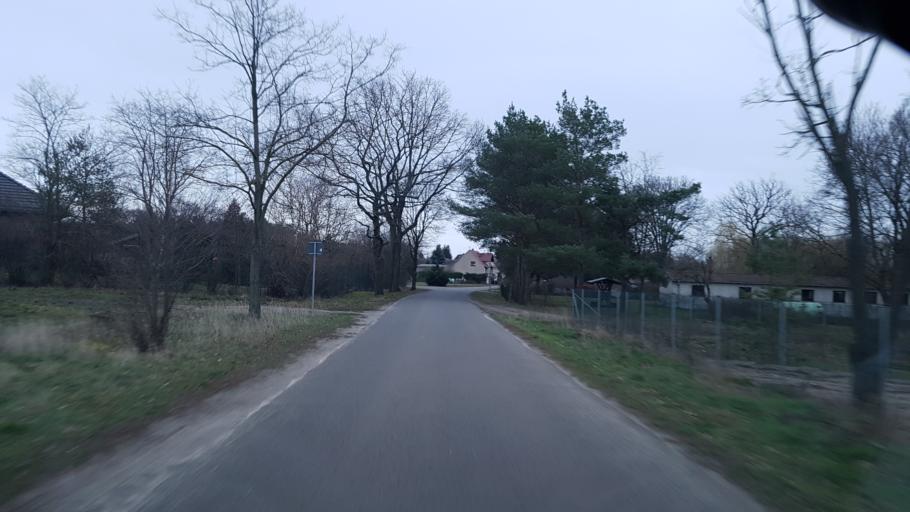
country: DE
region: Brandenburg
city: Schlieben
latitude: 51.6981
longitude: 13.3260
